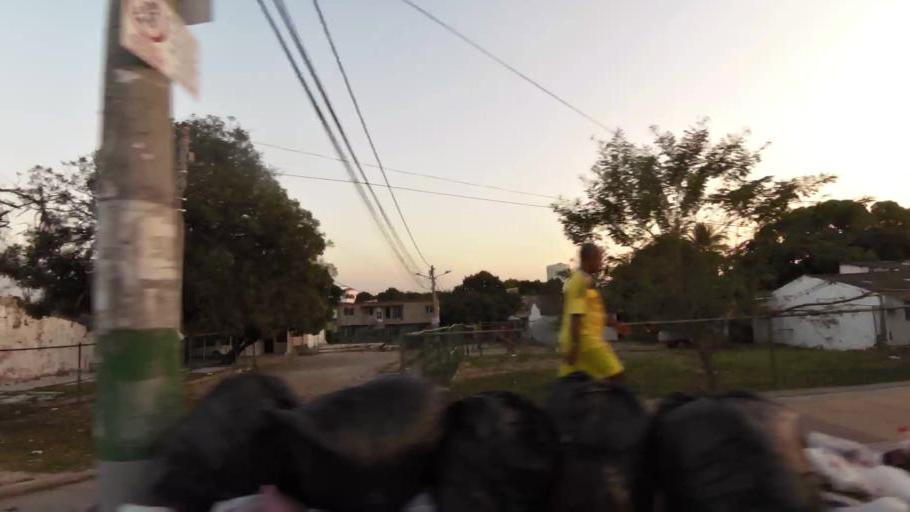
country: CO
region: Bolivar
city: Cartagena
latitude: 10.3904
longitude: -75.4900
